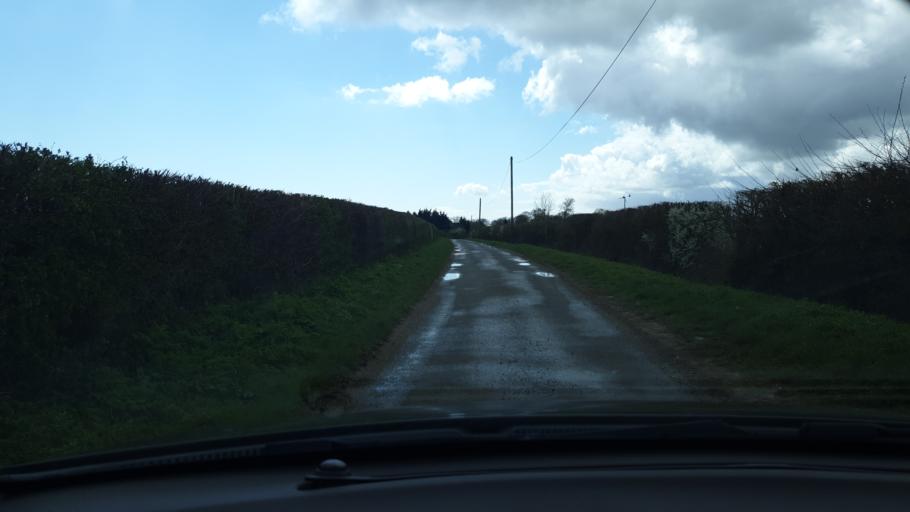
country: GB
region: England
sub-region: Essex
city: Mistley
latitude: 51.8950
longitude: 1.1320
